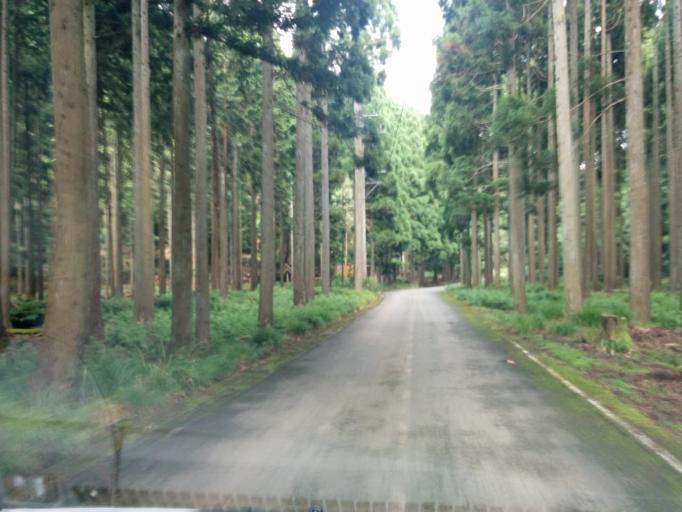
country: JP
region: Kyoto
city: Miyazu
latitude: 35.4601
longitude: 135.1196
